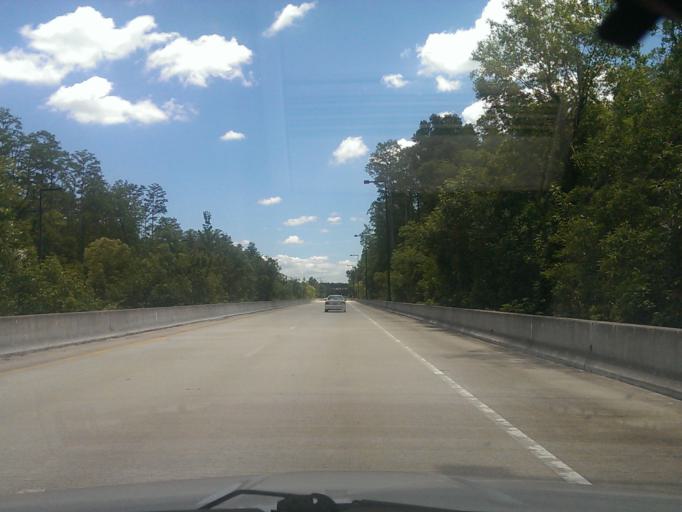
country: US
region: Florida
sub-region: Osceola County
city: Celebration
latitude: 28.3644
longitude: -81.5831
